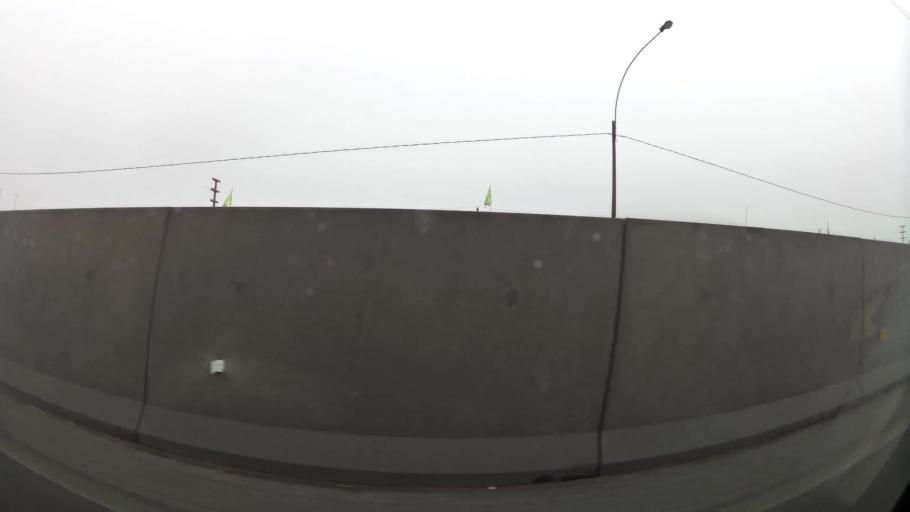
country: PE
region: Lima
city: Ventanilla
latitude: -11.8327
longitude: -77.1145
